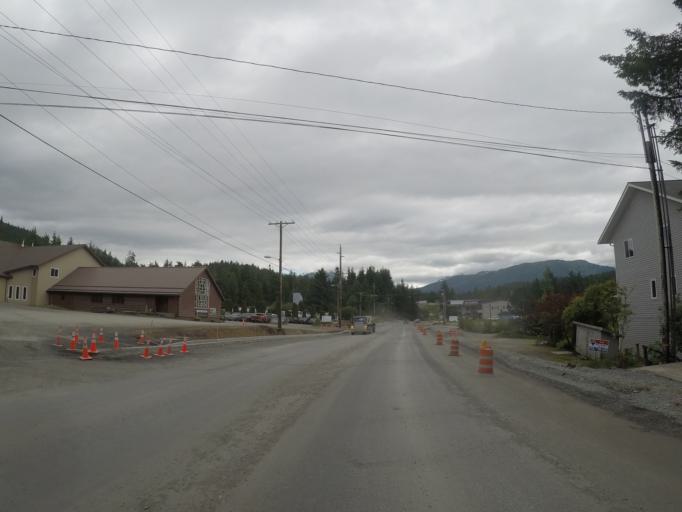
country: US
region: Alaska
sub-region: Juneau City and Borough
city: Juneau
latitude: 58.3870
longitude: -134.6525
